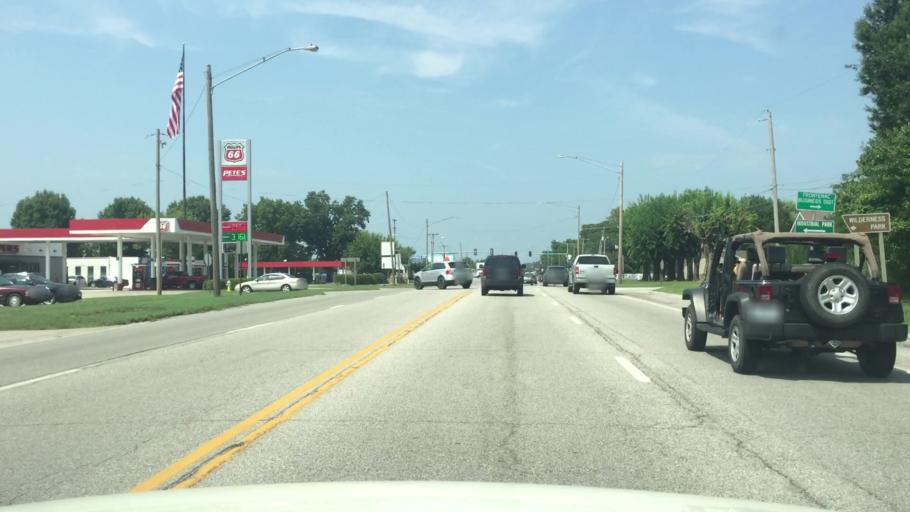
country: US
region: Kansas
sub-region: Crawford County
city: Frontenac
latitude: 37.4532
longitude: -94.7051
